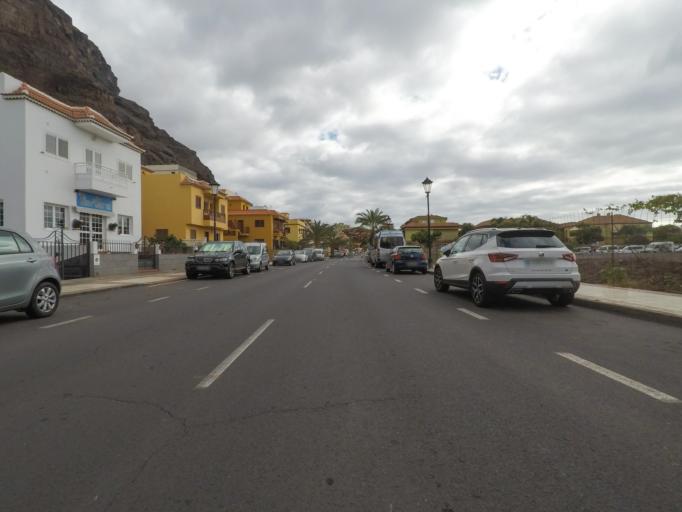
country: ES
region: Canary Islands
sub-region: Provincia de Santa Cruz de Tenerife
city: Alajero
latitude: 28.0869
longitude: -17.3350
